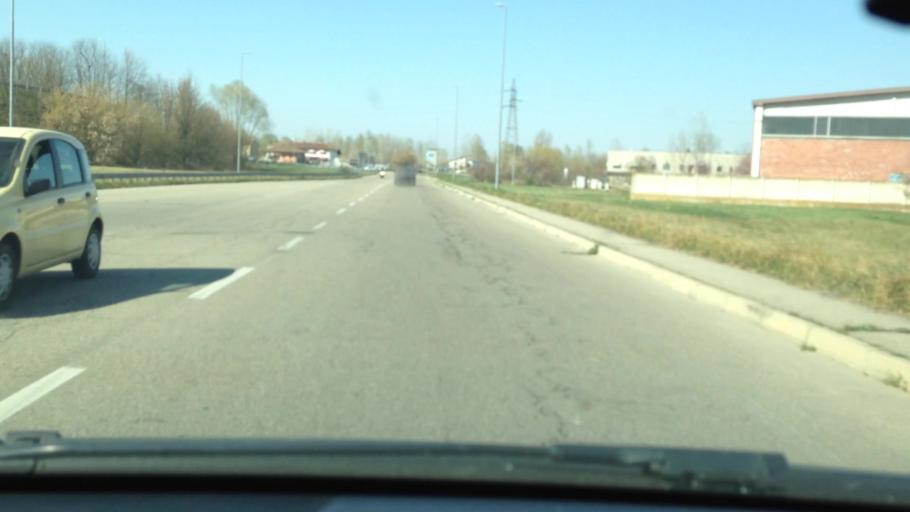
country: IT
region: Piedmont
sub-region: Provincia di Asti
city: Asti
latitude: 44.9180
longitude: 8.2287
